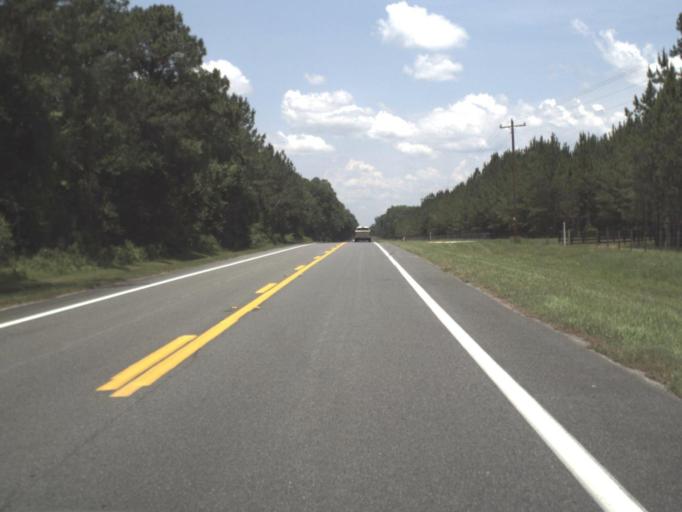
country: US
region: Florida
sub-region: Union County
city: Lake Butler
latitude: 30.0474
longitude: -82.3977
